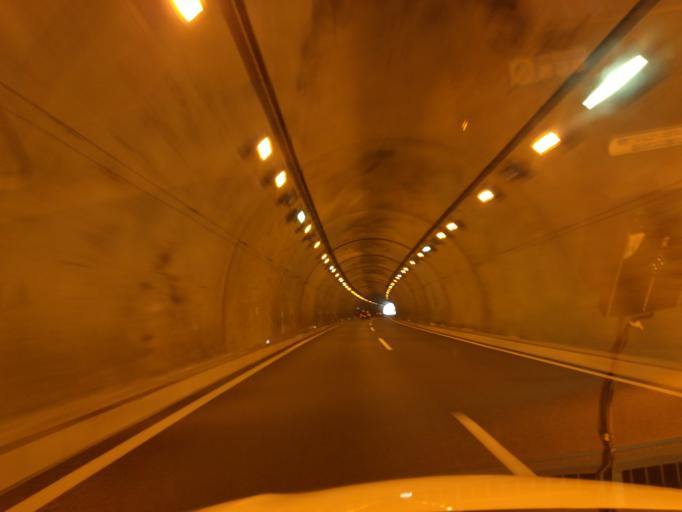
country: JP
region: Ehime
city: Kawanoecho
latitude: 33.7997
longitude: 133.6613
